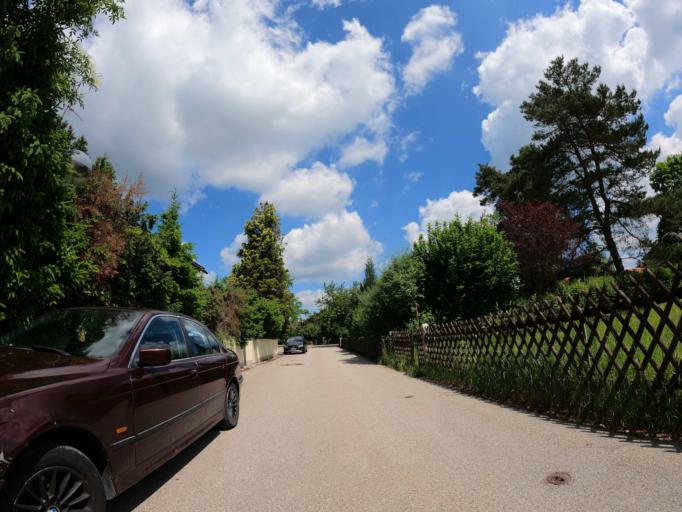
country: DE
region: Bavaria
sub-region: Upper Bavaria
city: Oberhaching
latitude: 47.9792
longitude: 11.5708
